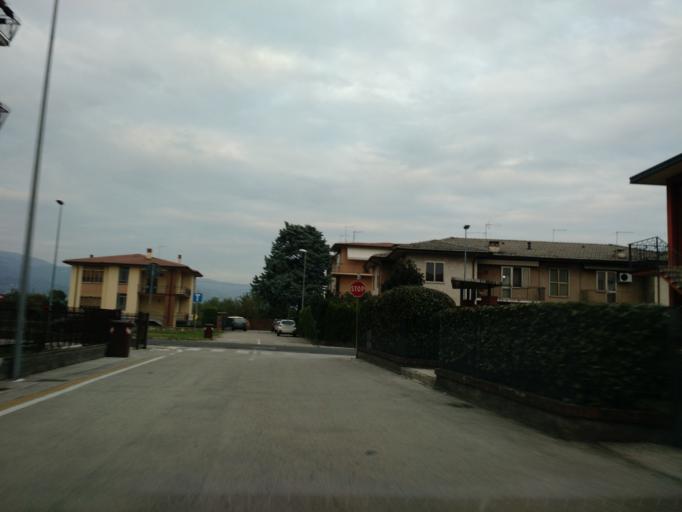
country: IT
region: Veneto
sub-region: Provincia di Vicenza
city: Thiene
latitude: 45.7133
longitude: 11.4899
